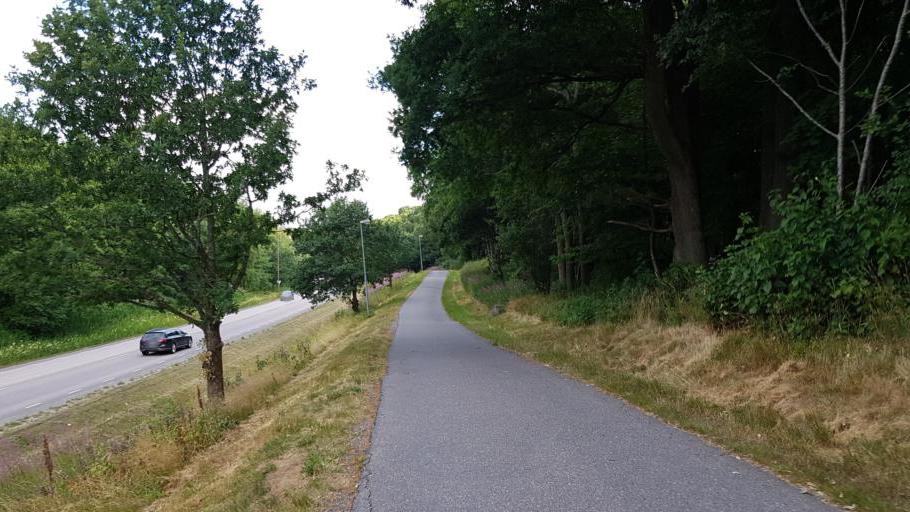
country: SE
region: Vaestra Goetaland
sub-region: Harryda Kommun
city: Molnlycke
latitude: 57.6582
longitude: 12.1051
